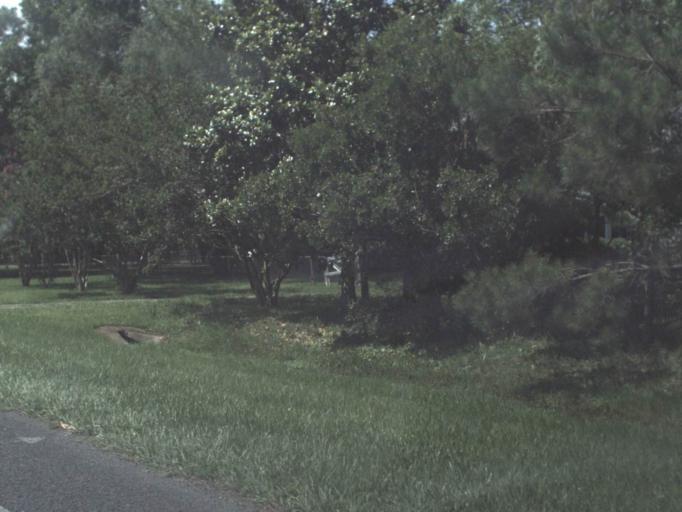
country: US
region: Florida
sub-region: Nassau County
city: Callahan
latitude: 30.5982
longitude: -81.8329
